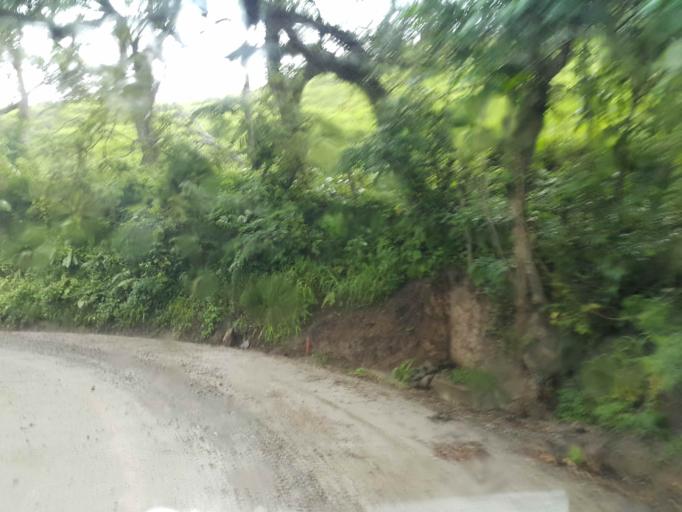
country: CR
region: Guanacaste
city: Juntas
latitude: 10.2307
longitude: -84.8504
